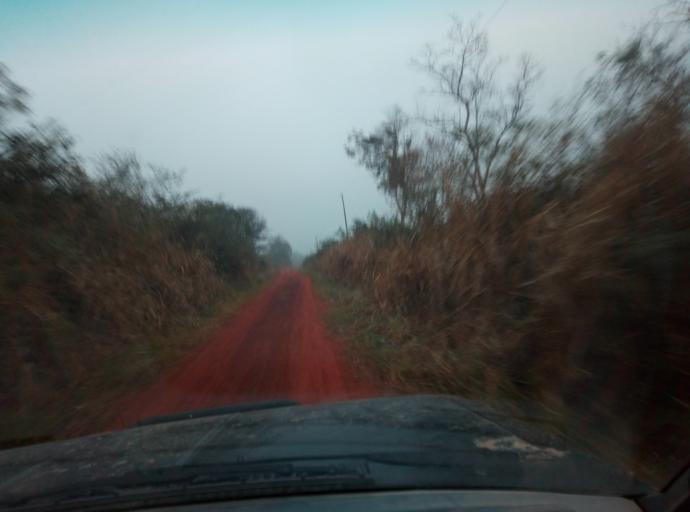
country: PY
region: Caaguazu
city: Doctor Cecilio Baez
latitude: -25.1590
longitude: -56.2580
